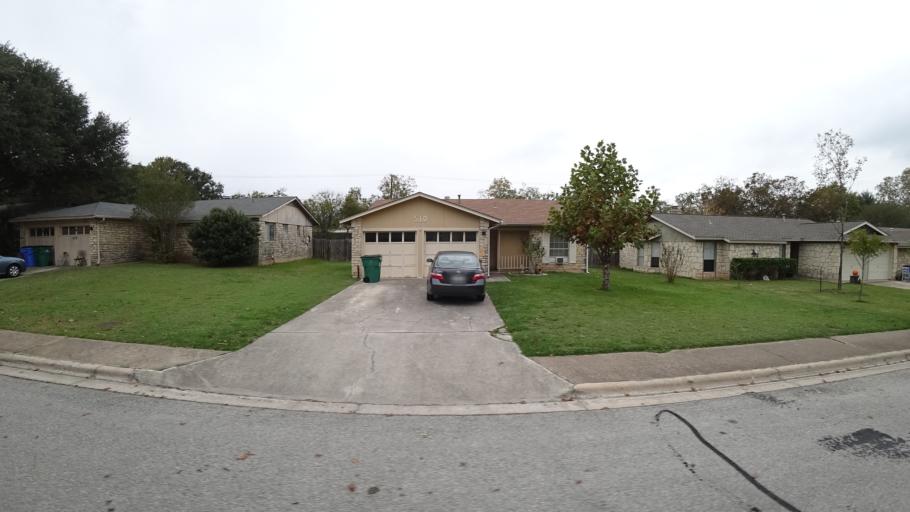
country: US
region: Texas
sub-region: Travis County
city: Pflugerville
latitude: 30.4312
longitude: -97.6122
